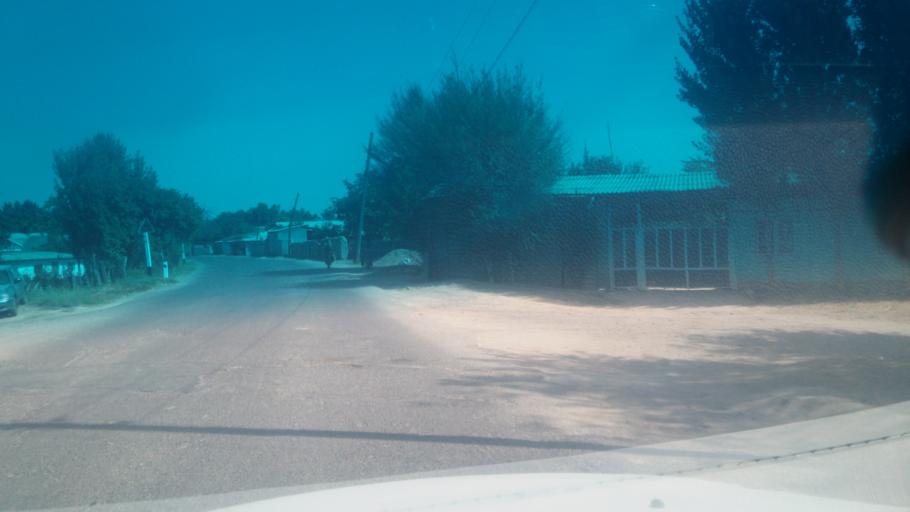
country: UZ
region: Sirdaryo
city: Sirdaryo
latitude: 40.8200
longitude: 68.6714
